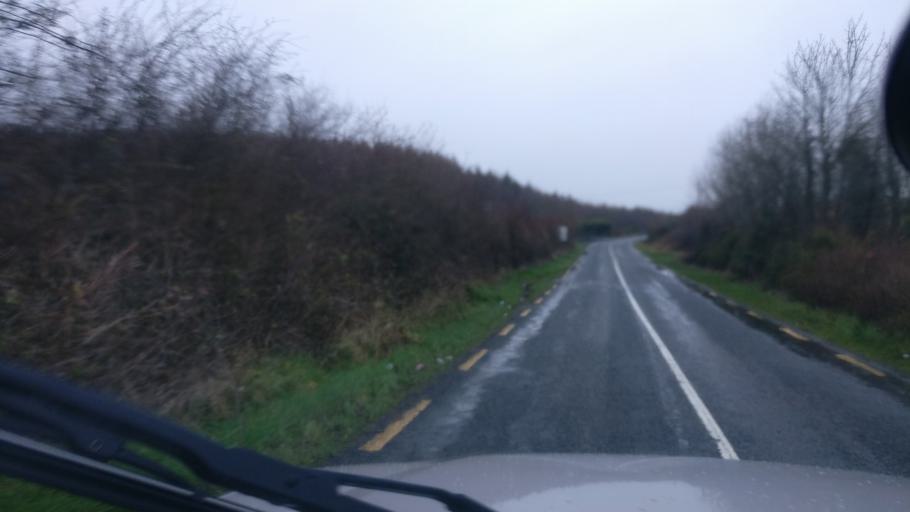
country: IE
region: Connaught
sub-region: County Galway
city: Loughrea
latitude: 53.1210
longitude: -8.4471
